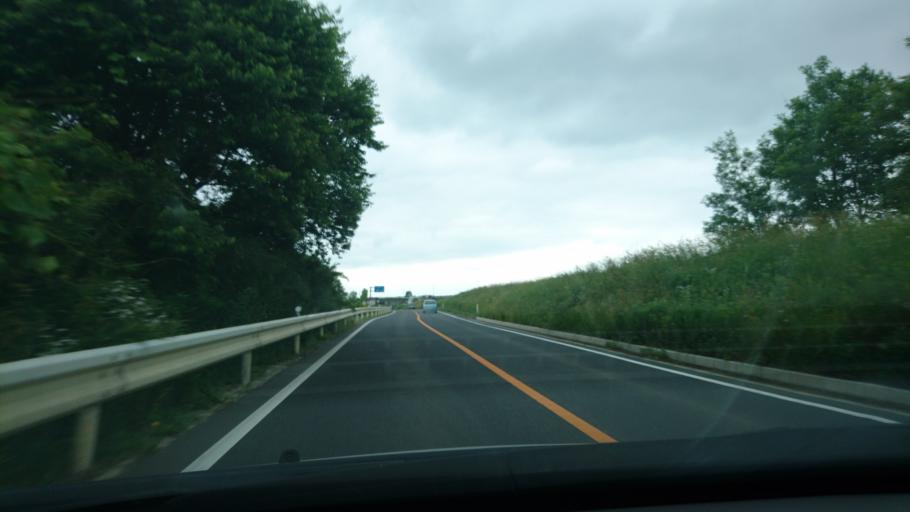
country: JP
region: Iwate
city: Ichinoseki
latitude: 38.7410
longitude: 141.1514
